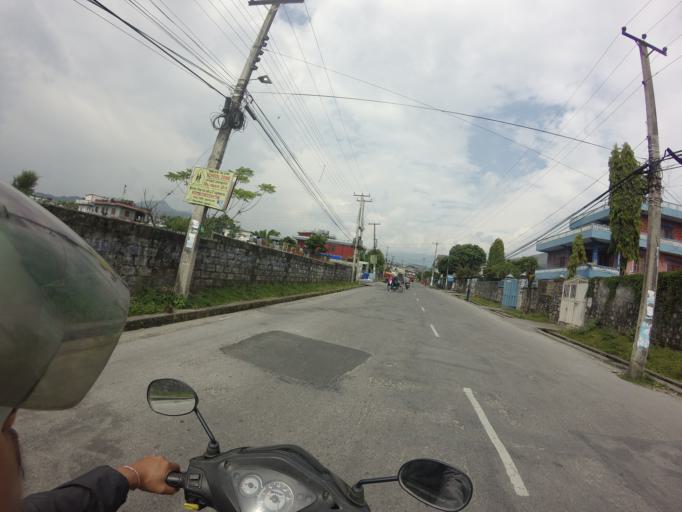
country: NP
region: Western Region
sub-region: Gandaki Zone
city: Pokhara
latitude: 28.2168
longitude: 83.9978
